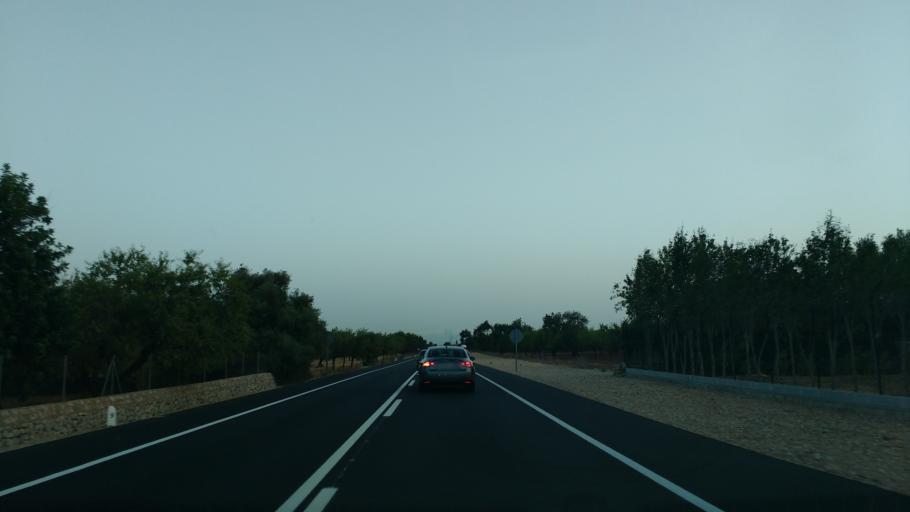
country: ES
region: Balearic Islands
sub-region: Illes Balears
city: Bunyola
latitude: 39.6726
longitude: 2.6782
